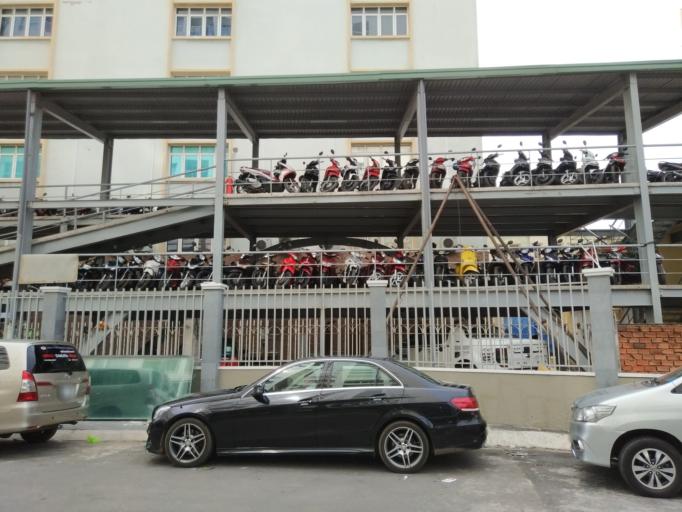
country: VN
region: Ho Chi Minh City
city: Quan Phu Nhuan
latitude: 10.8059
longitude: 106.6657
